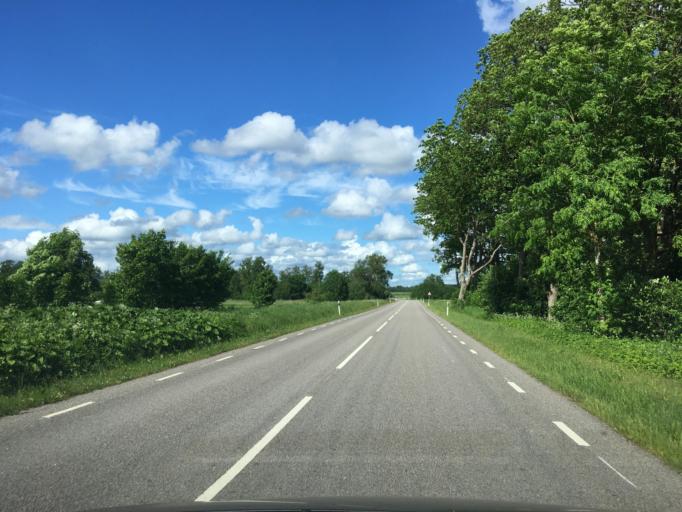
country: EE
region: Paernumaa
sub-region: Halinga vald
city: Parnu-Jaagupi
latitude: 58.6484
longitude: 24.5639
